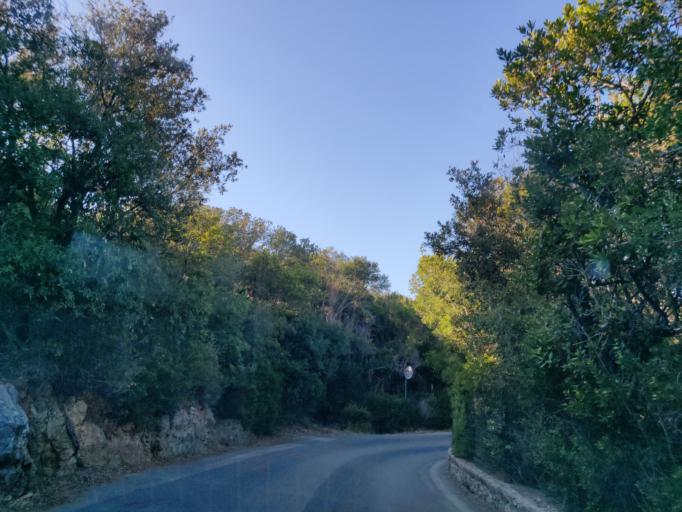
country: IT
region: Tuscany
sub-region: Provincia di Grosseto
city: Orbetello Scalo
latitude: 42.4102
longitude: 11.2917
